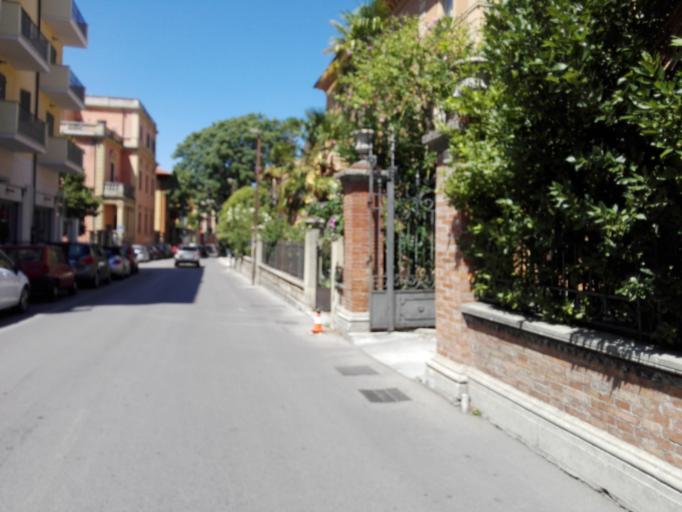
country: IT
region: Umbria
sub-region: Provincia di Perugia
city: Foligno
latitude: 42.9526
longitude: 12.7046
